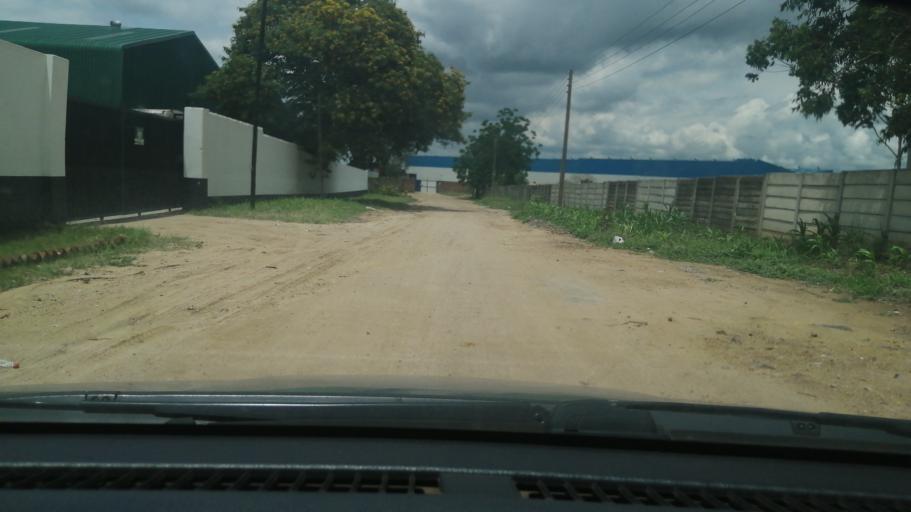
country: ZW
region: Harare
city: Harare
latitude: -17.8755
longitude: 31.0228
